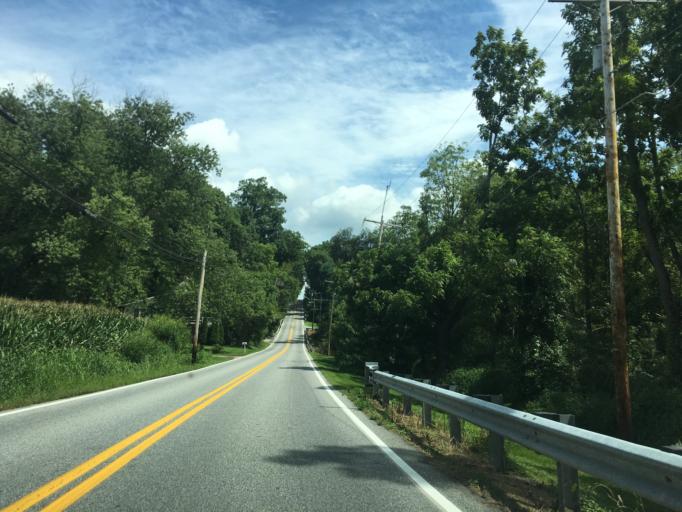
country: US
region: Pennsylvania
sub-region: York County
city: New Freedom
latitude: 39.7137
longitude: -76.6694
